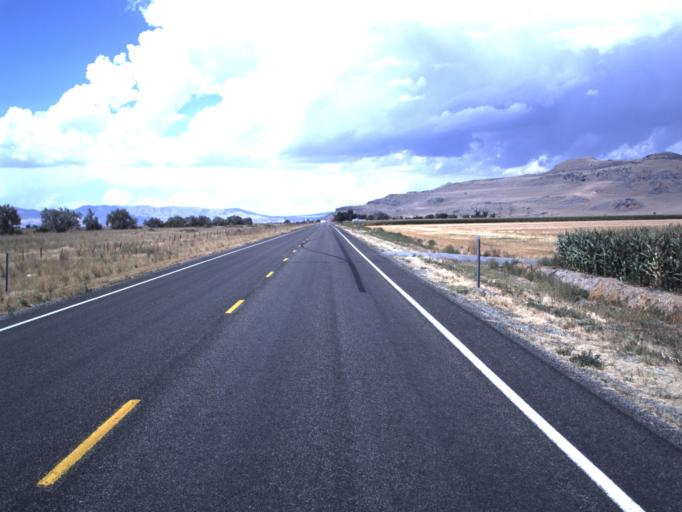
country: US
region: Utah
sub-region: Box Elder County
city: Honeyville
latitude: 41.5663
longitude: -112.1832
